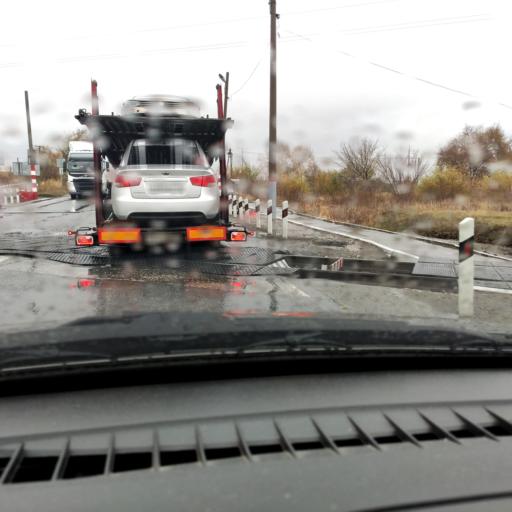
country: RU
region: Samara
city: Tol'yatti
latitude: 53.5616
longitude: 49.3566
